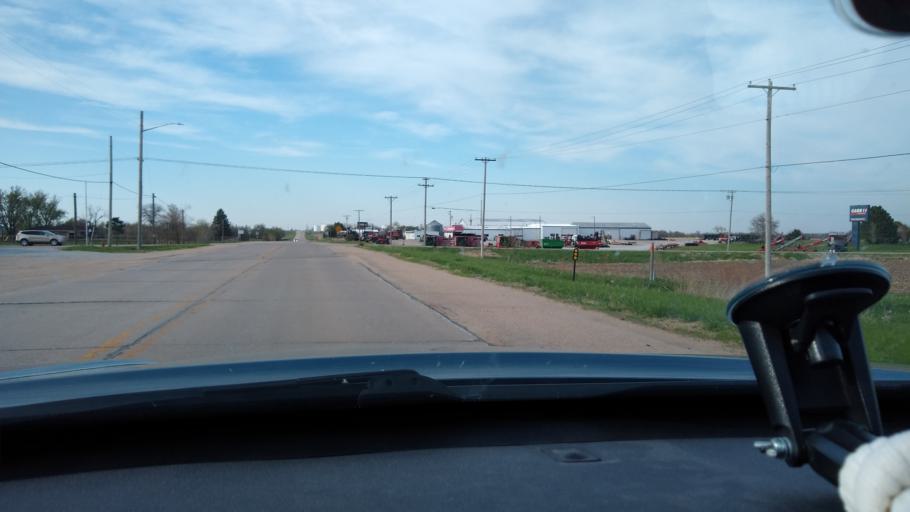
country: US
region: Nebraska
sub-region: Fillmore County
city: Geneva
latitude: 40.5380
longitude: -97.5958
